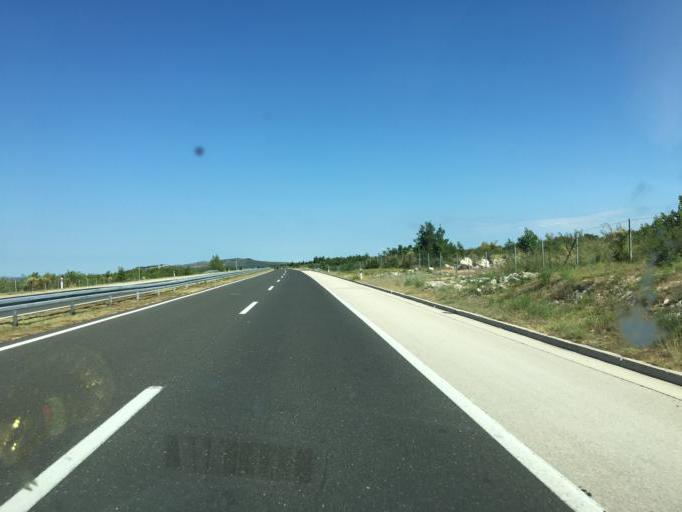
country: HR
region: Zadarska
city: Polaca
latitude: 44.0359
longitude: 15.5600
